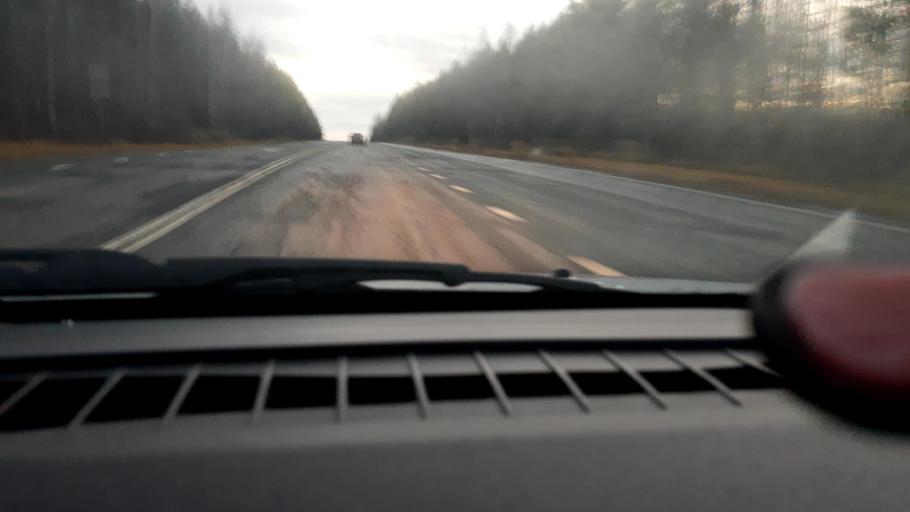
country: RU
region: Nizjnij Novgorod
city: Vladimirskoye
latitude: 56.9700
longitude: 45.1111
